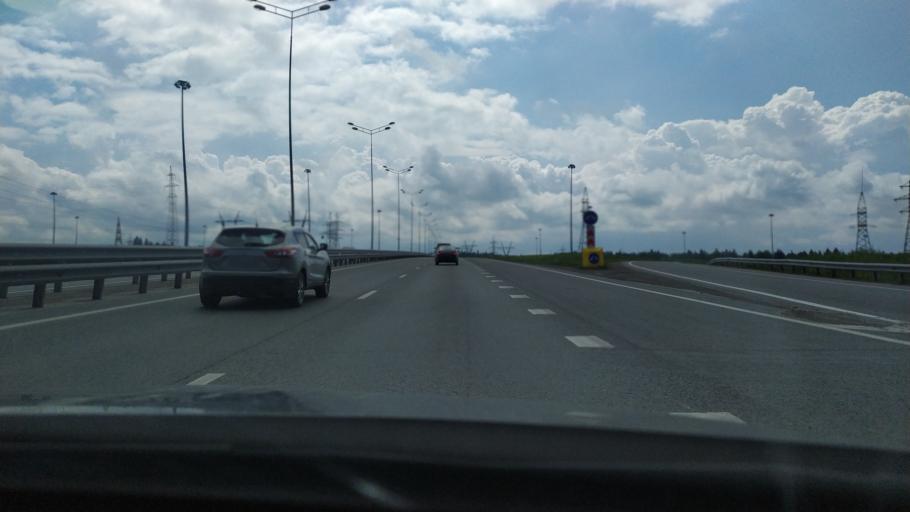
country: RU
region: Perm
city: Novyye Lyady
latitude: 58.0489
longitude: 56.4294
